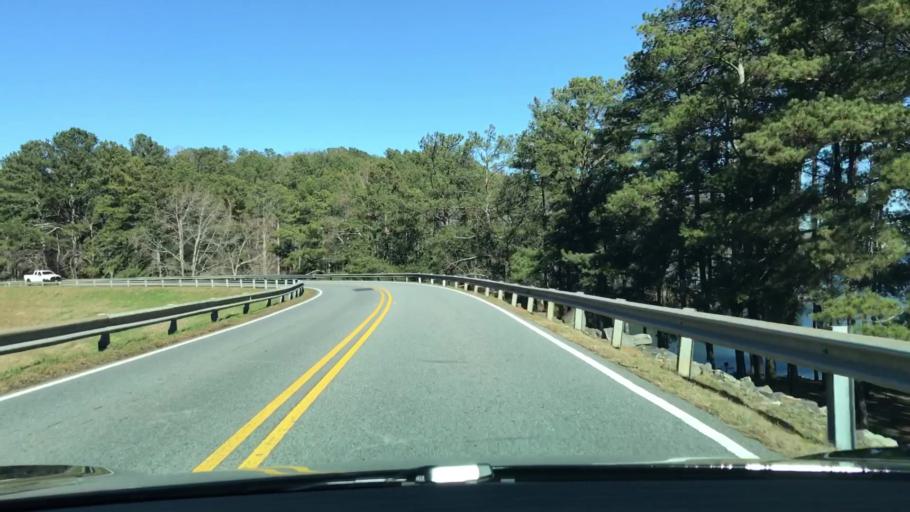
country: US
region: Georgia
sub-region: Forsyth County
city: Cumming
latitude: 34.1725
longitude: -84.0780
